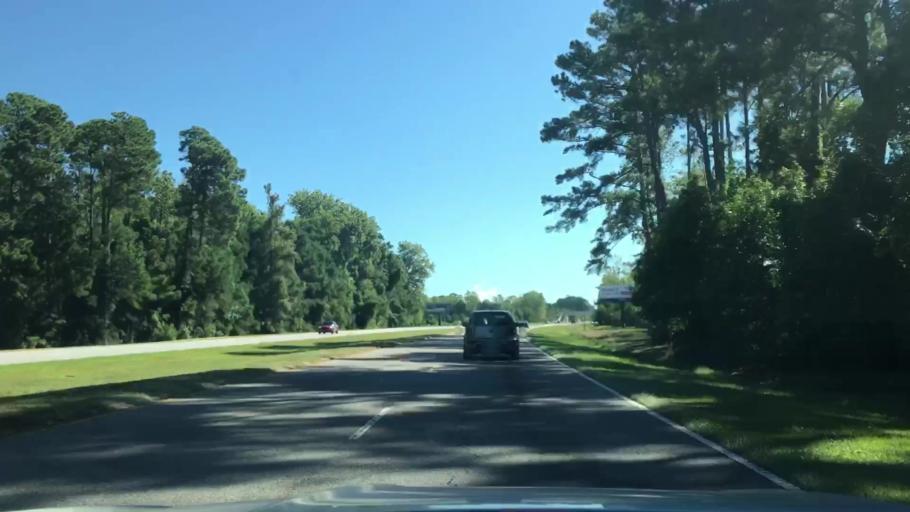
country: US
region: South Carolina
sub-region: Horry County
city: Myrtle Beach
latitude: 33.7365
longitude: -78.8572
